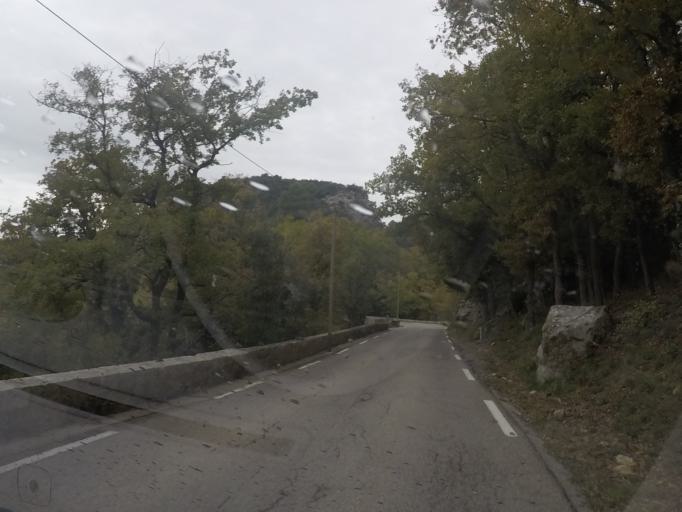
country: FR
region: Provence-Alpes-Cote d'Azur
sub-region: Departement du Vaucluse
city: Bonnieux
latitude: 43.8117
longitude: 5.3400
